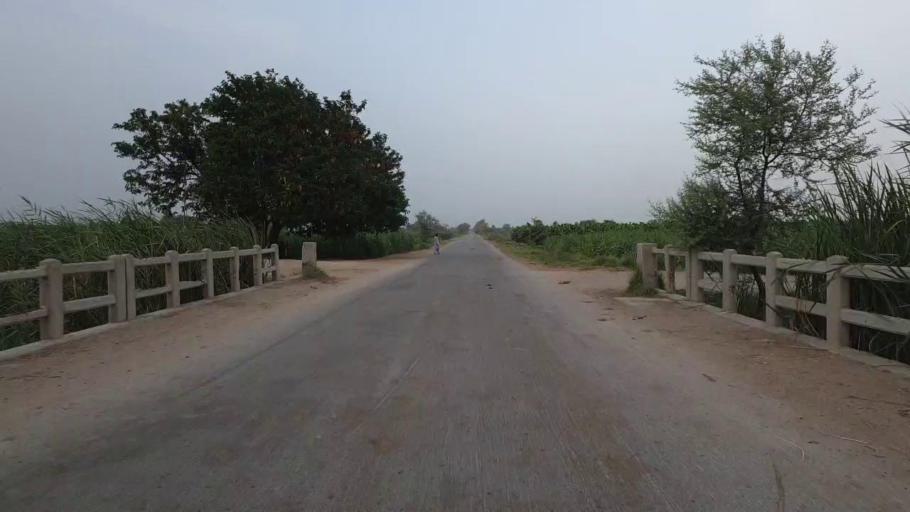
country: PK
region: Sindh
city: Daur
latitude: 26.4043
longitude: 68.2253
